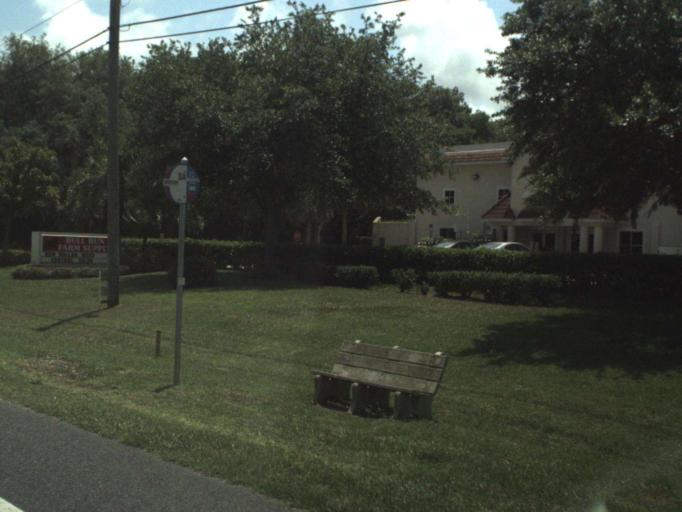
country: US
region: Florida
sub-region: Volusia County
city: Ormond Beach
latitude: 29.3085
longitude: -81.0978
